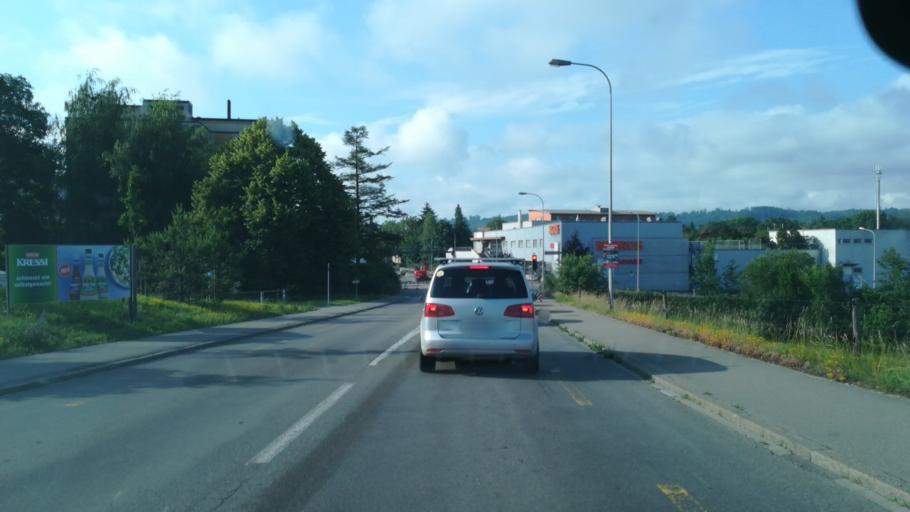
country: CH
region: Thurgau
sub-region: Weinfelden District
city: Sulgen
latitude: 47.5415
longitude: 9.1829
